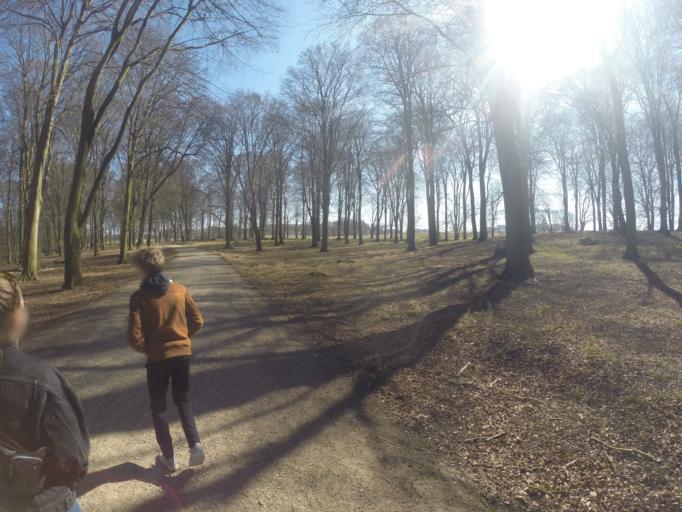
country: DK
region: Capital Region
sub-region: Rudersdal Kommune
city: Trorod
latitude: 55.8024
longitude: 12.5656
